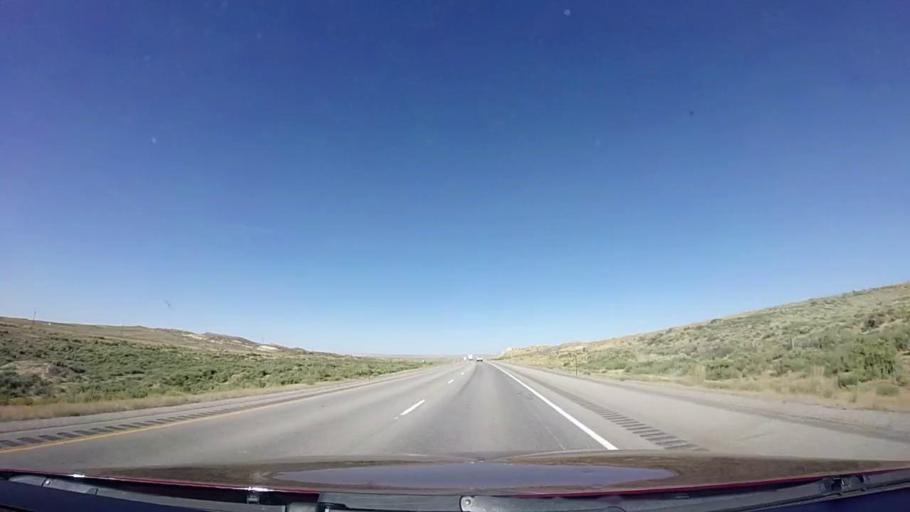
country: US
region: Wyoming
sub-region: Carbon County
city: Rawlins
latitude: 41.7888
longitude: -107.3935
